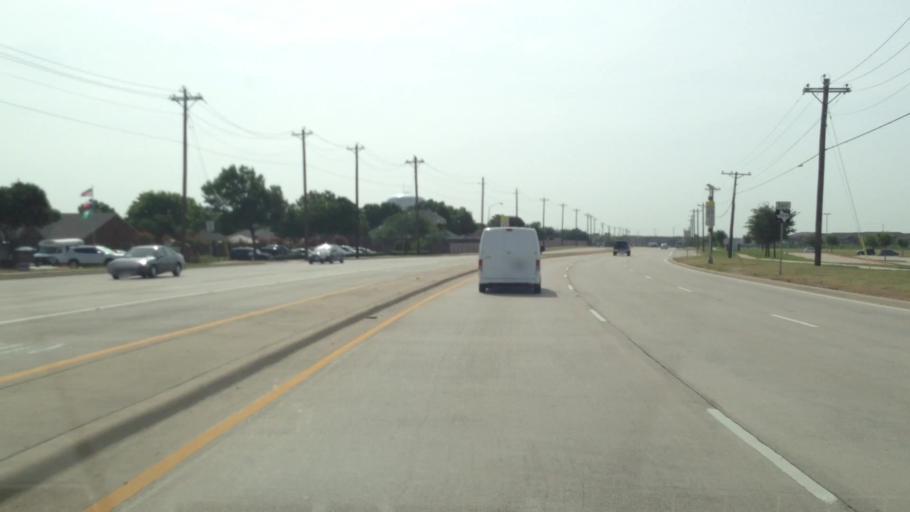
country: US
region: Texas
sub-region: Denton County
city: Lewisville
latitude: 33.0096
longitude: -97.0274
